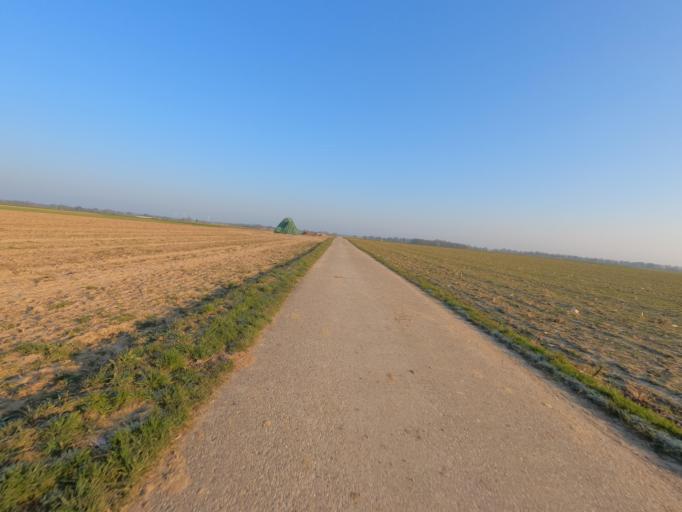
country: DE
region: North Rhine-Westphalia
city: Huckelhoven
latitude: 51.0736
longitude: 6.2621
